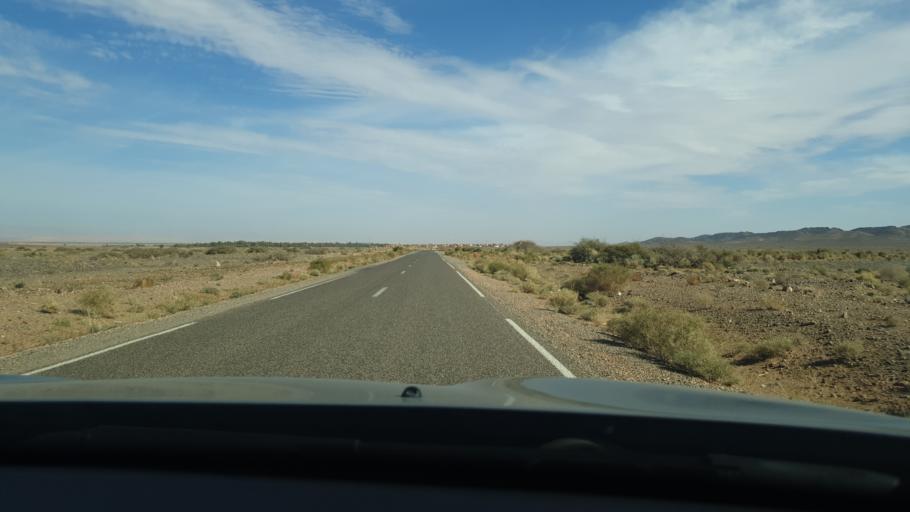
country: MA
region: Meknes-Tafilalet
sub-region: Errachidia
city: Goulmima
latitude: 31.5137
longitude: -4.9856
